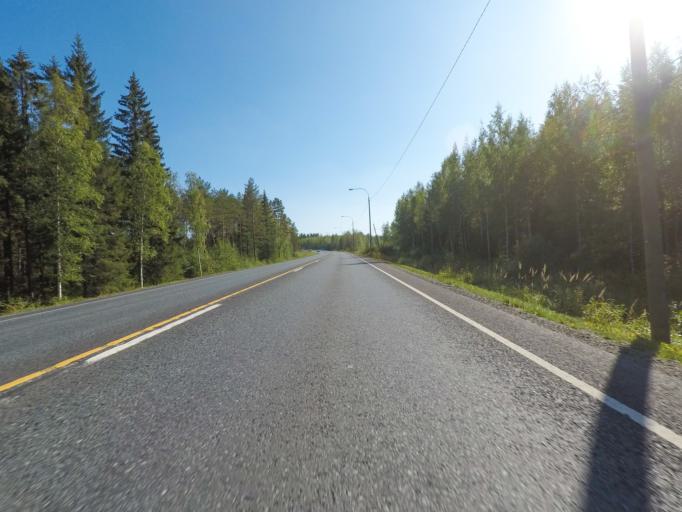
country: FI
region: Northern Savo
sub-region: Varkaus
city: Leppaevirta
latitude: 62.5482
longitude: 27.6230
